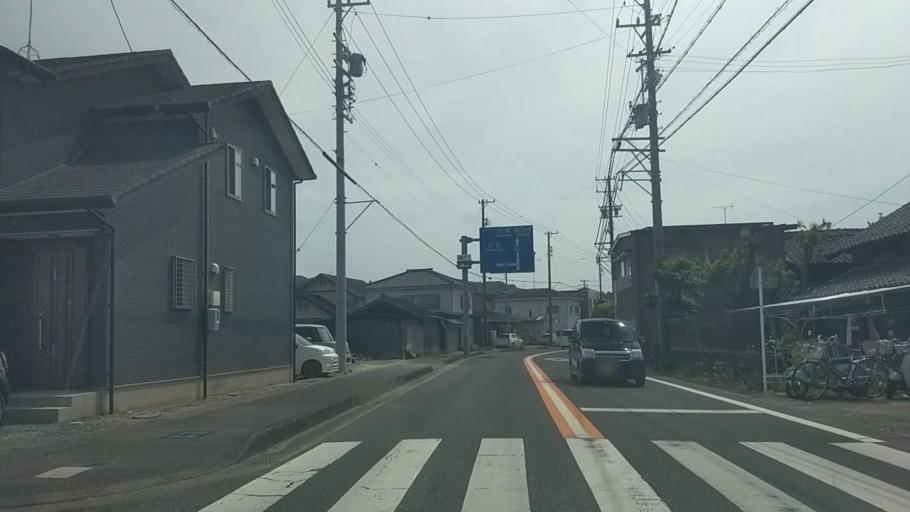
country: JP
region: Shizuoka
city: Hamamatsu
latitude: 34.7886
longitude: 137.6459
